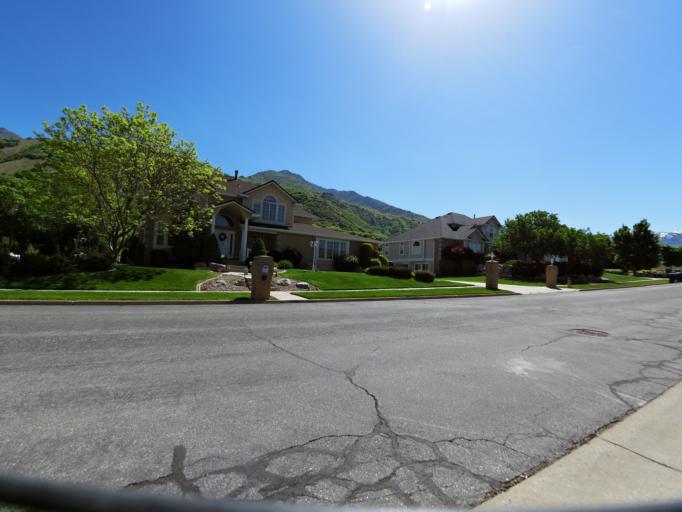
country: US
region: Utah
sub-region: Weber County
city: Uintah
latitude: 41.1656
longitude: -111.9275
